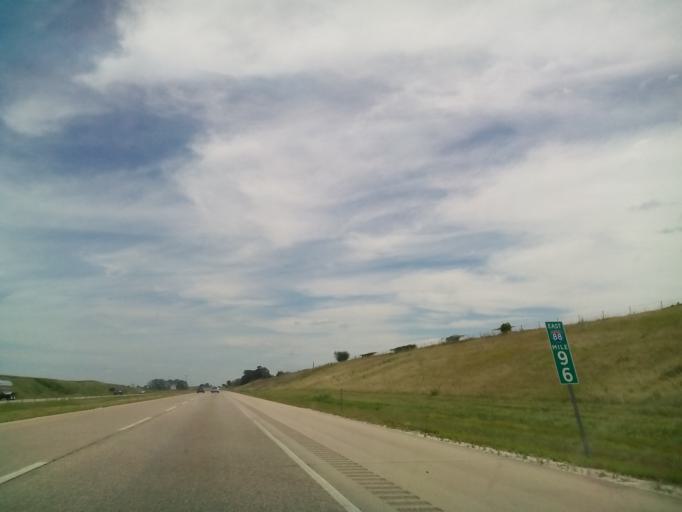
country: US
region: Illinois
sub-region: DeKalb County
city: Cortland
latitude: 41.9006
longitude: -88.6864
